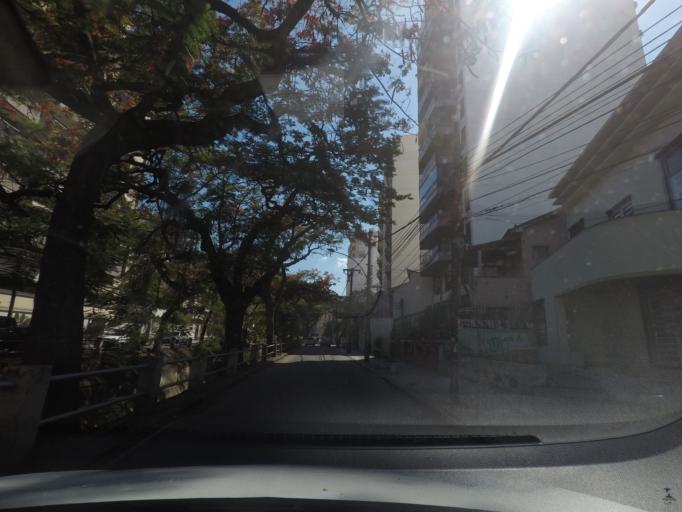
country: BR
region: Rio de Janeiro
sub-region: Rio De Janeiro
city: Rio de Janeiro
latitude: -22.9293
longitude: -43.2410
